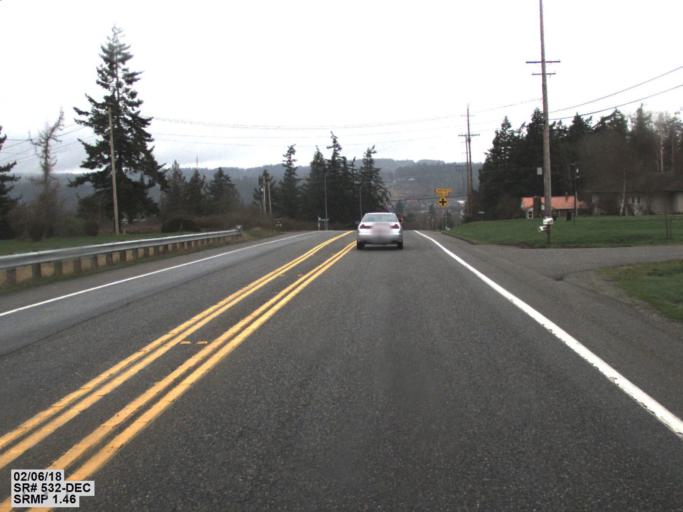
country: US
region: Washington
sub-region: Snohomish County
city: Stanwood
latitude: 48.2398
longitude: -122.4257
